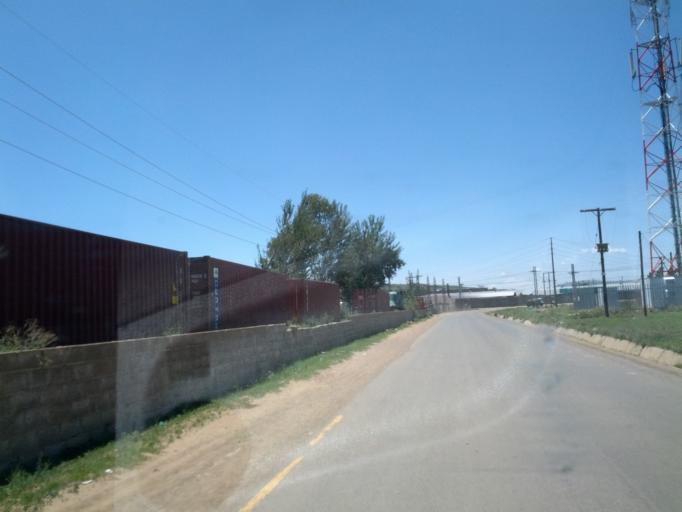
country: LS
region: Maseru
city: Maseru
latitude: -29.2969
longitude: 27.4631
